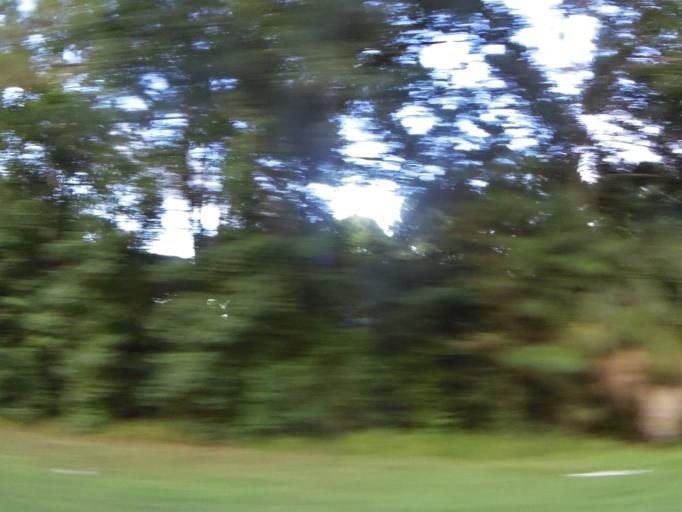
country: US
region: Florida
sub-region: Duval County
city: Jacksonville
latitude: 30.2485
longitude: -81.5547
